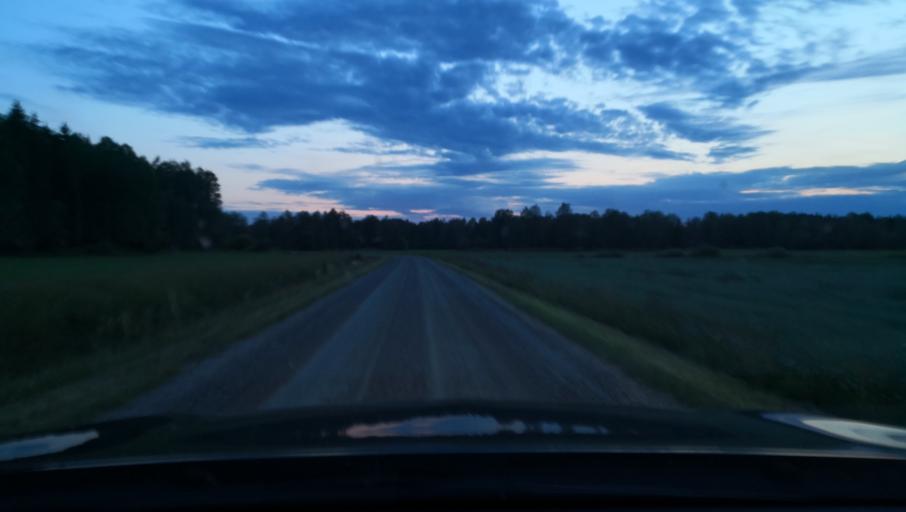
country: SE
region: Uppsala
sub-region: Heby Kommun
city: OEstervala
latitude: 60.0145
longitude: 17.3030
